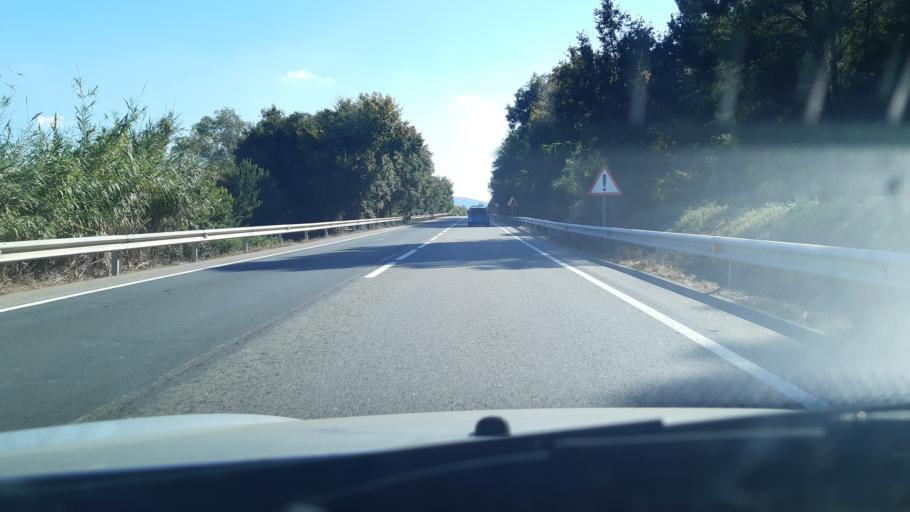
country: ES
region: Catalonia
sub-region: Provincia de Tarragona
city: Tivenys
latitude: 40.8639
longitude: 0.5067
